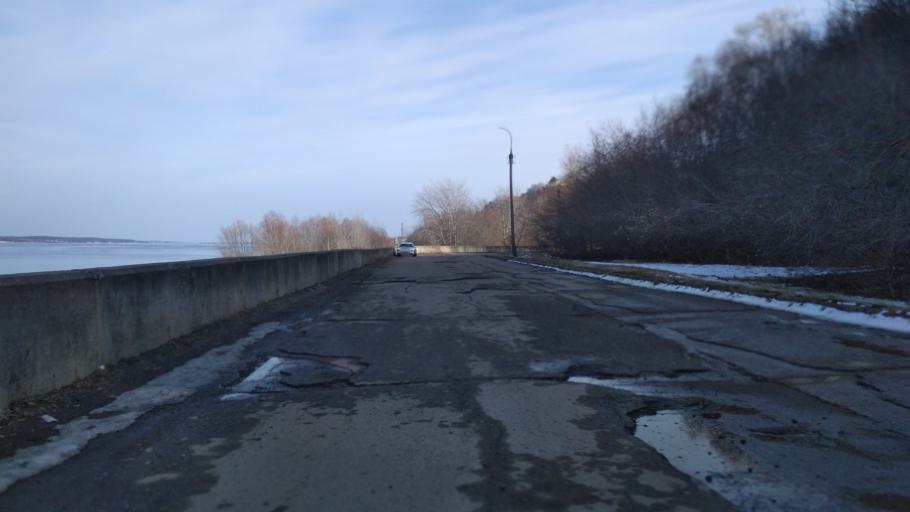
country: RU
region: Chuvashia
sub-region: Cheboksarskiy Rayon
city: Cheboksary
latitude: 56.1486
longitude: 47.2920
